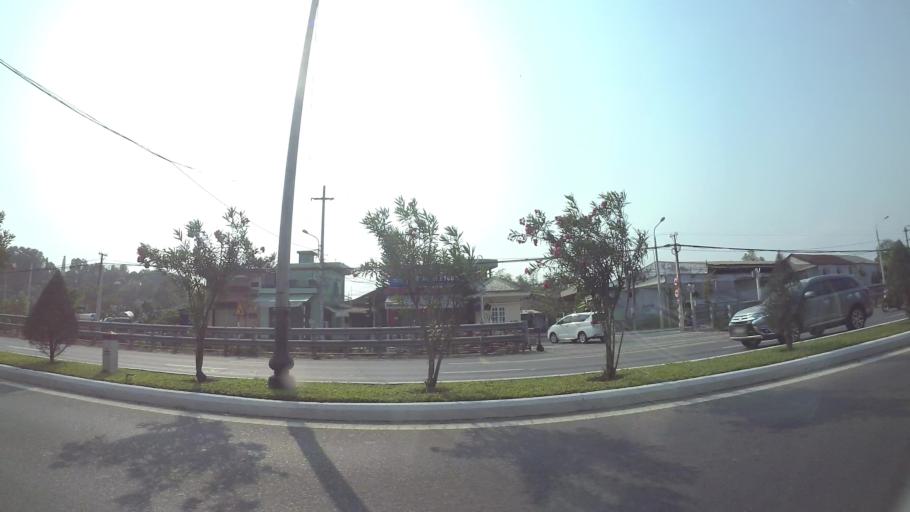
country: VN
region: Da Nang
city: Cam Le
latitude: 16.0173
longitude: 108.1935
